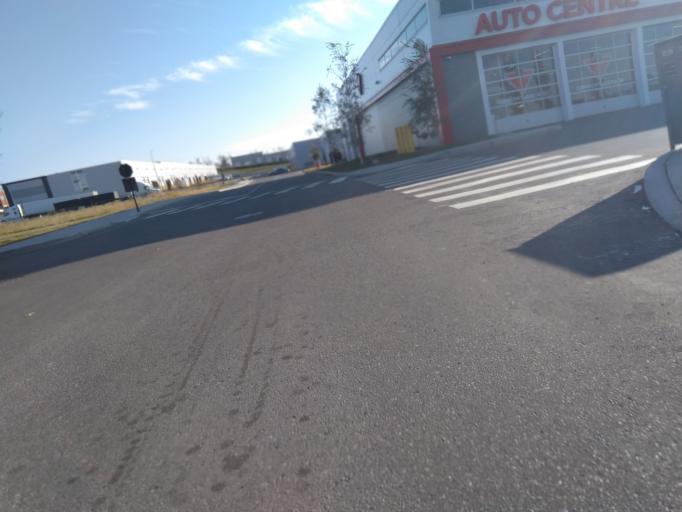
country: CA
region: Alberta
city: Calgary
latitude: 51.1067
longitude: -114.0413
